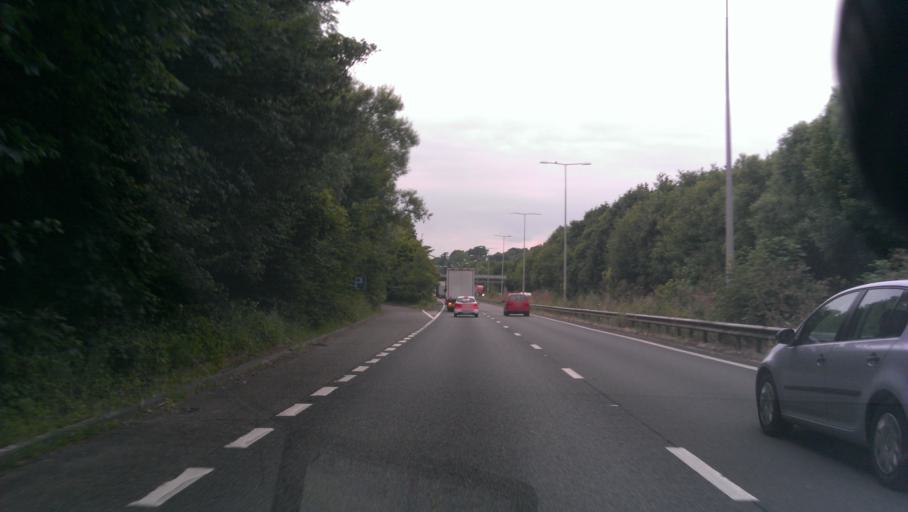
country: GB
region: England
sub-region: Kent
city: Dunkirk
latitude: 51.2964
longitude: 0.9458
